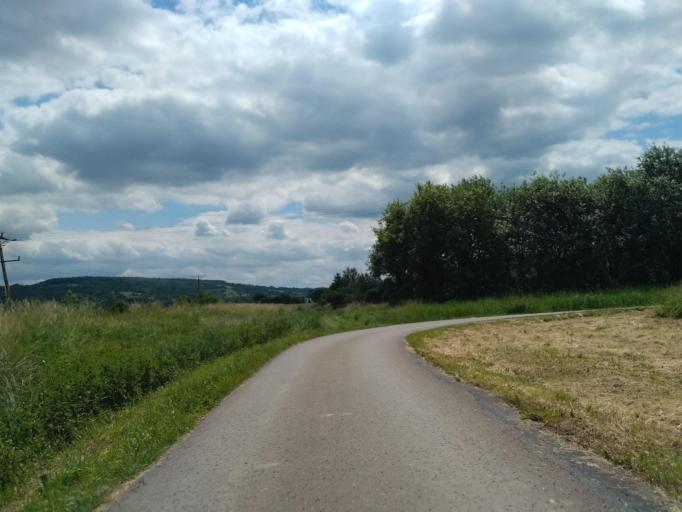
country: PL
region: Subcarpathian Voivodeship
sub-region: Powiat rzeszowski
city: Dynow
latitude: 49.8174
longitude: 22.2380
